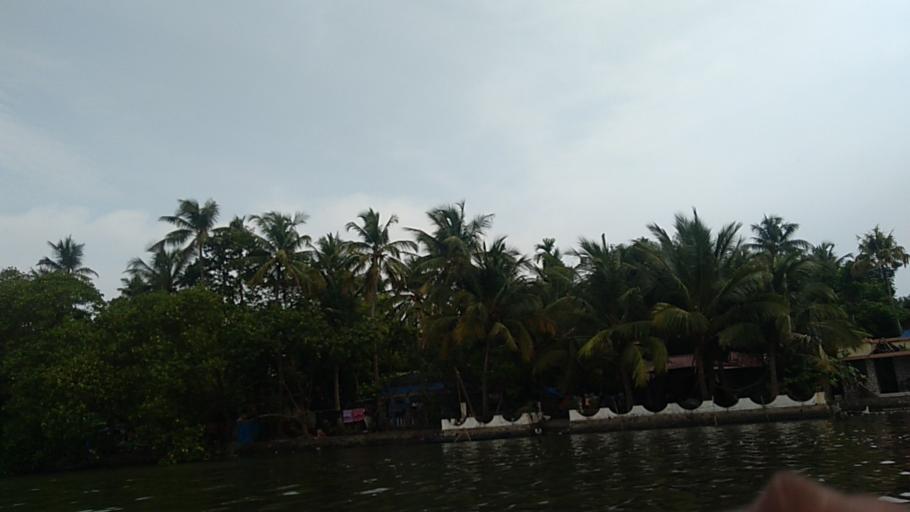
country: IN
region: Kerala
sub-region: Ernakulam
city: Elur
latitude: 10.0725
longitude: 76.2434
